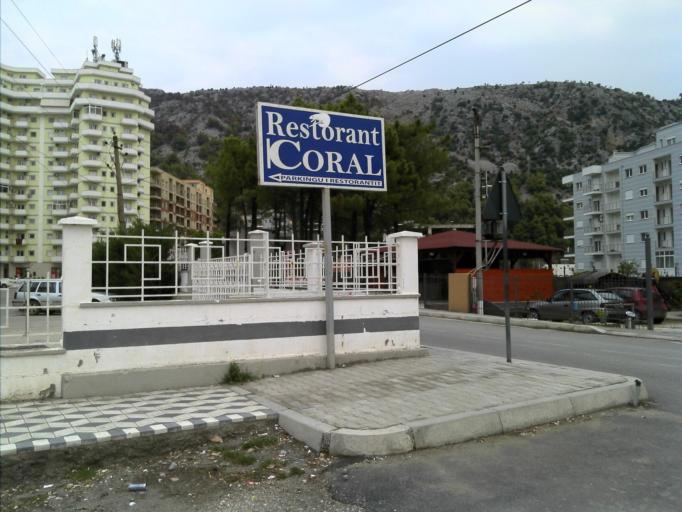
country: AL
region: Lezhe
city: Shengjin
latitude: 41.8063
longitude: 19.5995
